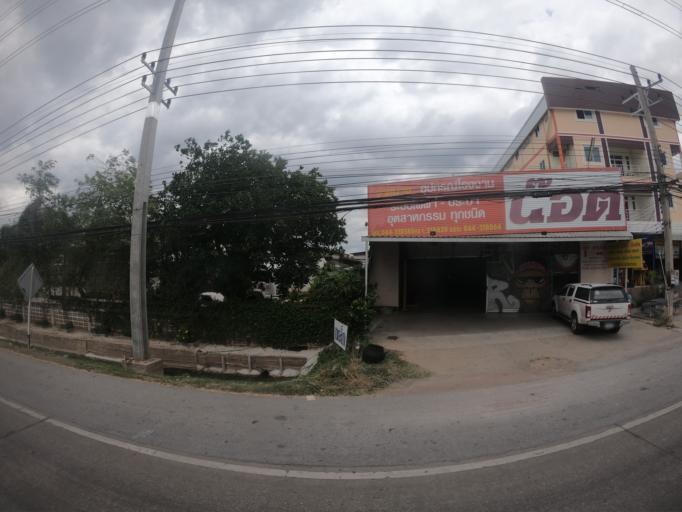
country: TH
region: Nakhon Ratchasima
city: Nakhon Ratchasima
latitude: 14.9189
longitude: 102.1467
